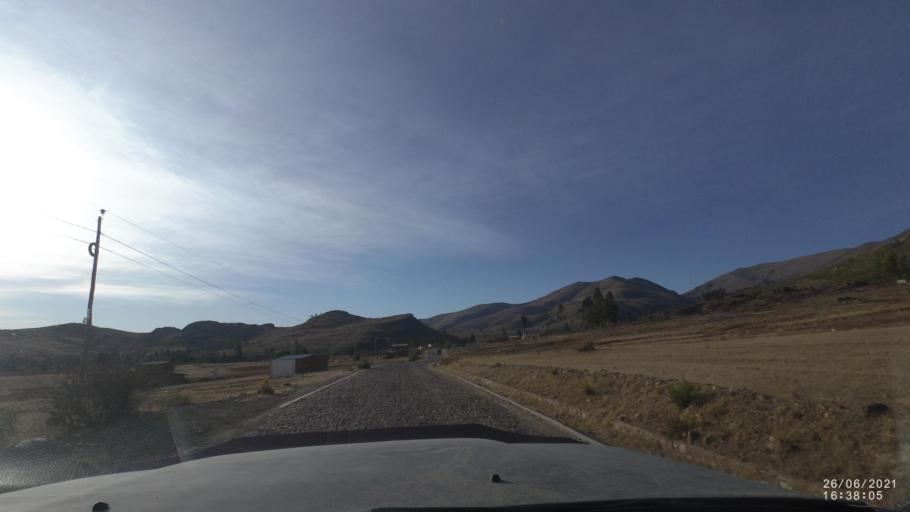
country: BO
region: Cochabamba
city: Arani
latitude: -17.7801
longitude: -65.8137
